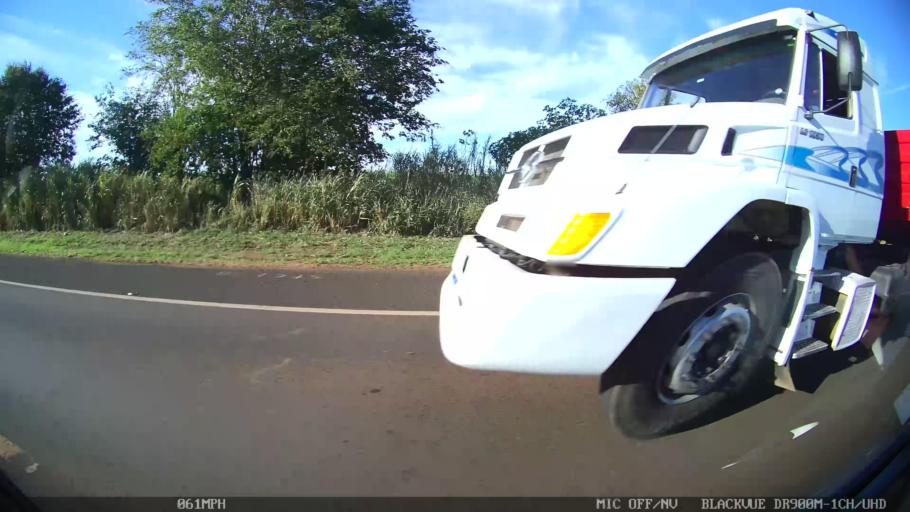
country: BR
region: Sao Paulo
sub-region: Americo Brasiliense
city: Americo Brasiliense
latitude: -21.7686
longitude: -48.1078
